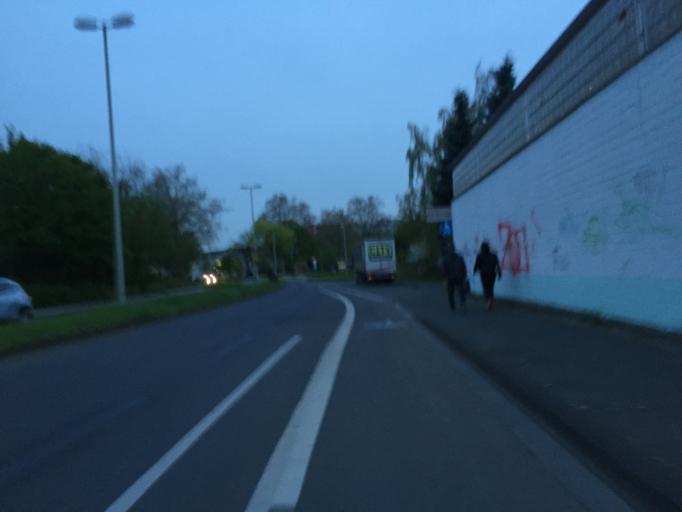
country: DE
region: North Rhine-Westphalia
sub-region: Regierungsbezirk Koln
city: Alfter
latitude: 50.7410
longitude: 7.0476
